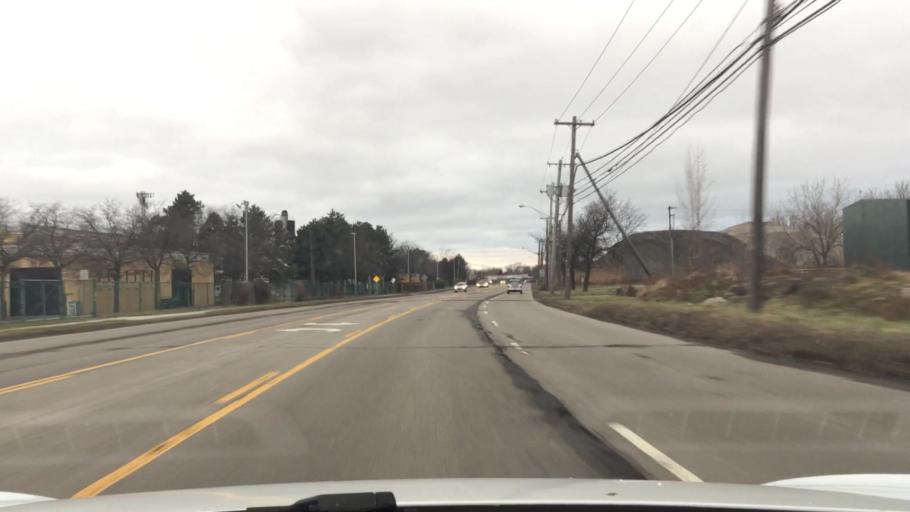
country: US
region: New York
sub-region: Erie County
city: Tonawanda
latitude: 43.0401
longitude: -78.8873
